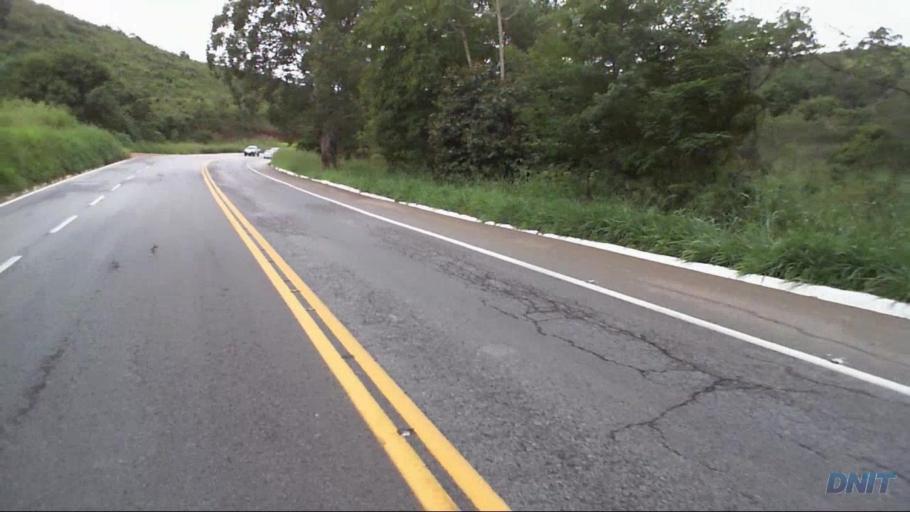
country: BR
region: Minas Gerais
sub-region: Joao Monlevade
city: Joao Monlevade
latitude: -19.8511
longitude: -43.2917
